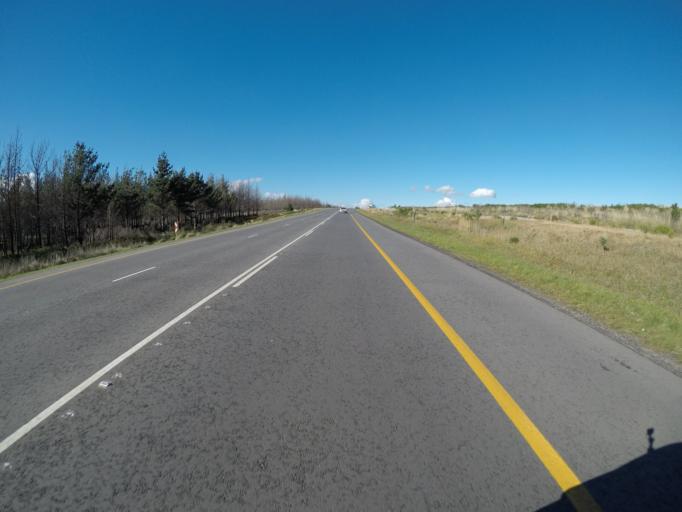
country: ZA
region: Western Cape
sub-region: Overberg District Municipality
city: Grabouw
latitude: -34.1524
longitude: 18.9629
